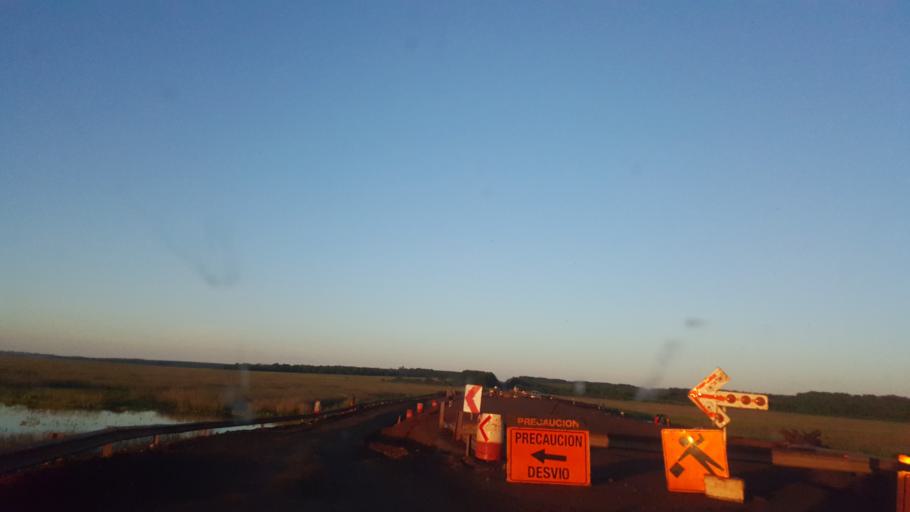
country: AR
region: Corrientes
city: Santo Tome
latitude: -28.3832
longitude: -55.9621
